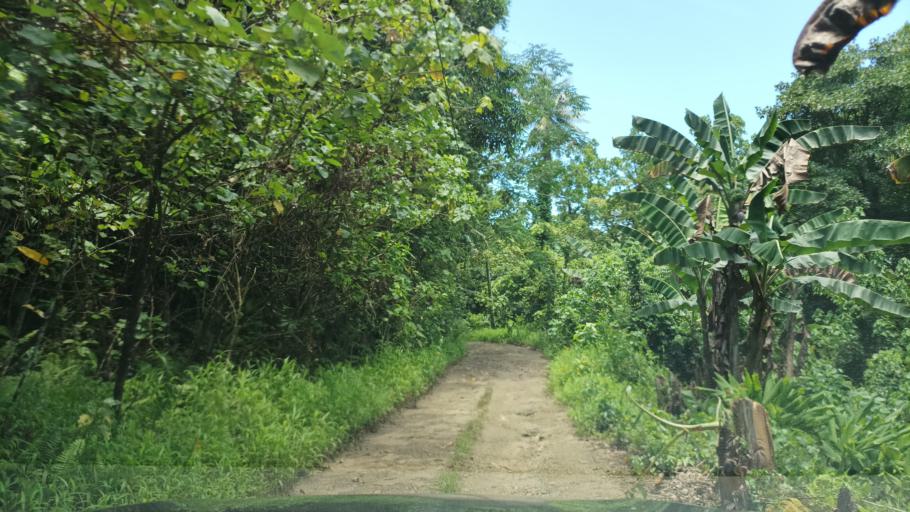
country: FM
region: Pohnpei
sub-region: Madolenihm Municipality
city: Madolenihm Municipality Government
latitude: 6.8438
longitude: 158.3186
